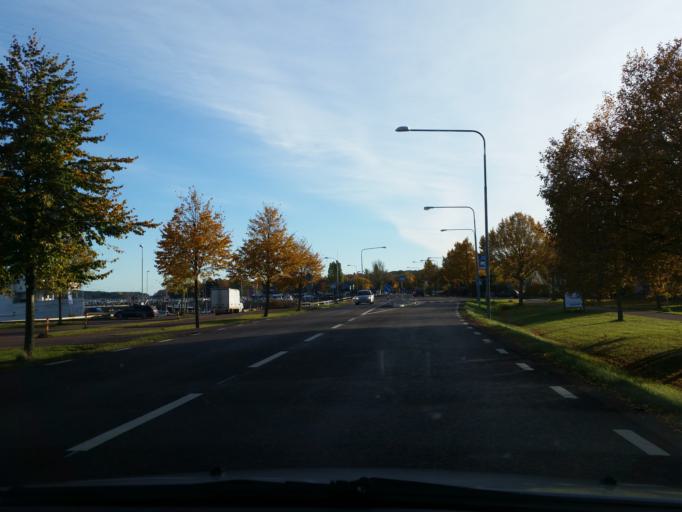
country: AX
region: Mariehamns stad
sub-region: Mariehamn
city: Mariehamn
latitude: 60.1034
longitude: 19.9449
